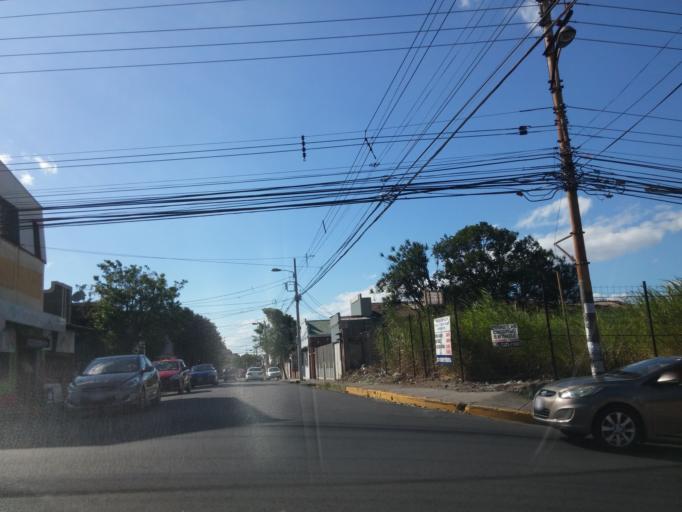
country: CR
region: San Jose
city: Colima
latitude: 9.9424
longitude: -84.0865
